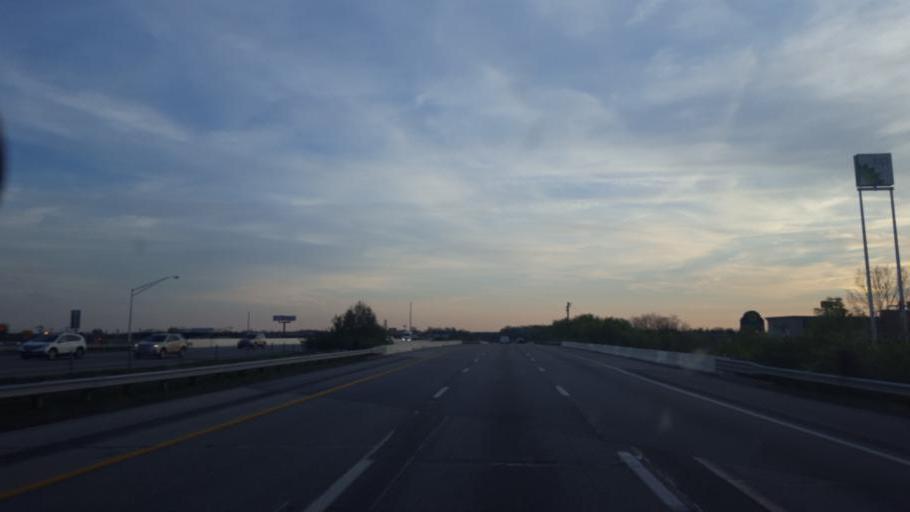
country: US
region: Ohio
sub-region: Hamilton County
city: Sixteen Mile Stand
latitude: 39.2947
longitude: -84.3147
